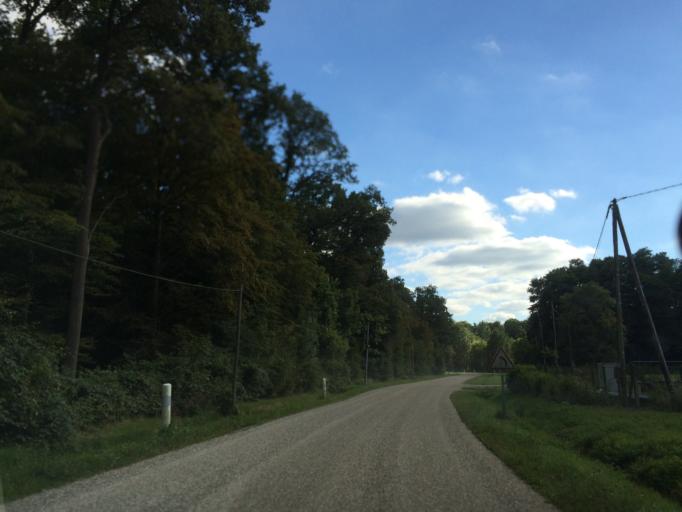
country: FR
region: Alsace
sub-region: Departement du Bas-Rhin
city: Betschdorf
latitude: 48.8864
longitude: 7.9217
